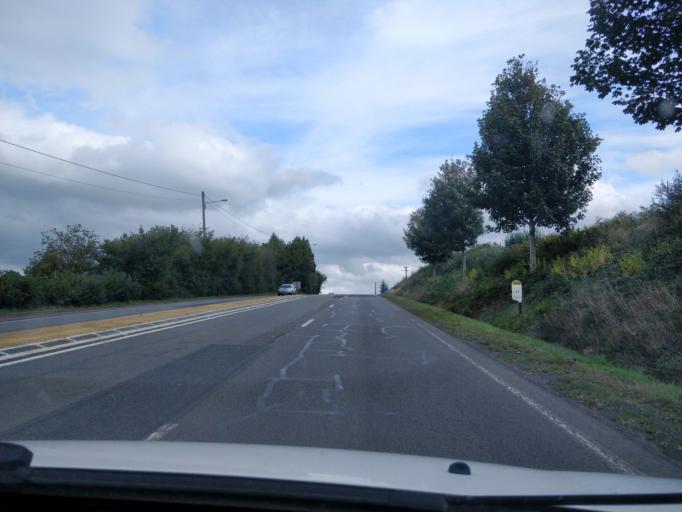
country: FR
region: Lower Normandy
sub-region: Departement du Calvados
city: Saint-Sever-Calvados
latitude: 48.8381
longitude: -1.0343
